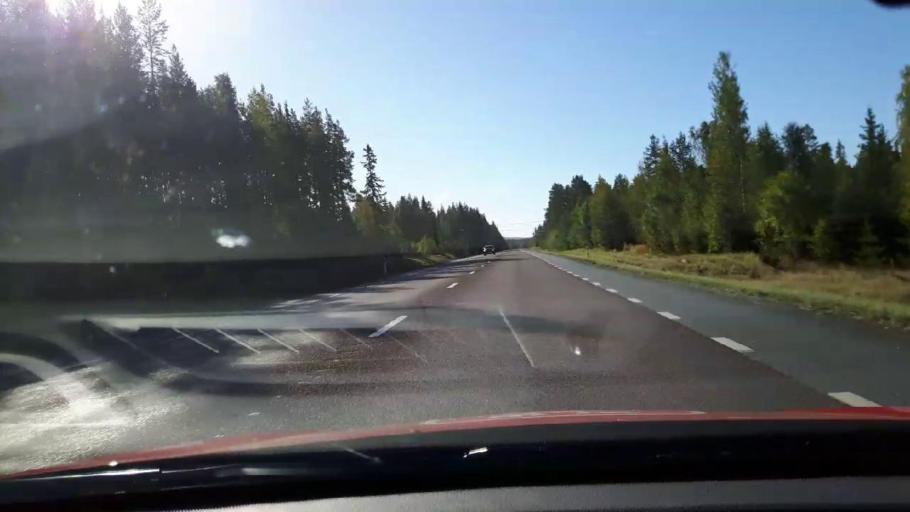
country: SE
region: Jaemtland
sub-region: Braecke Kommun
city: Braecke
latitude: 62.8633
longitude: 15.3120
